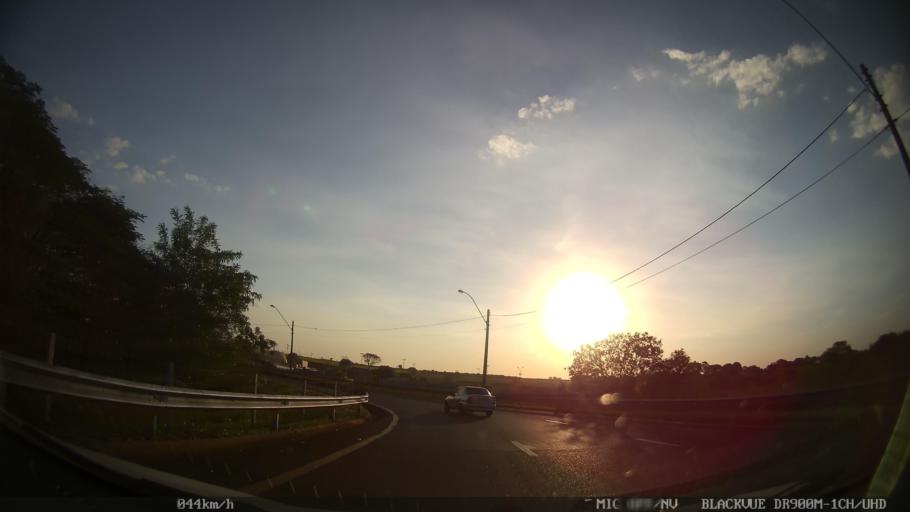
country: BR
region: Sao Paulo
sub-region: Ribeirao Preto
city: Ribeirao Preto
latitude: -21.1046
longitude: -47.8098
